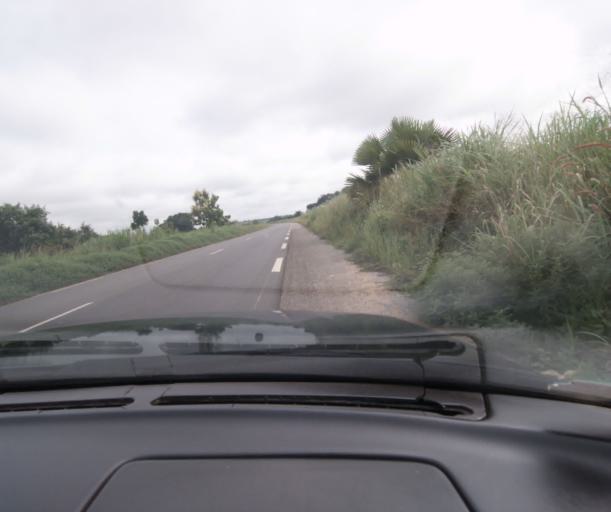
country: CM
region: Centre
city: Saa
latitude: 4.3852
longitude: 11.2557
